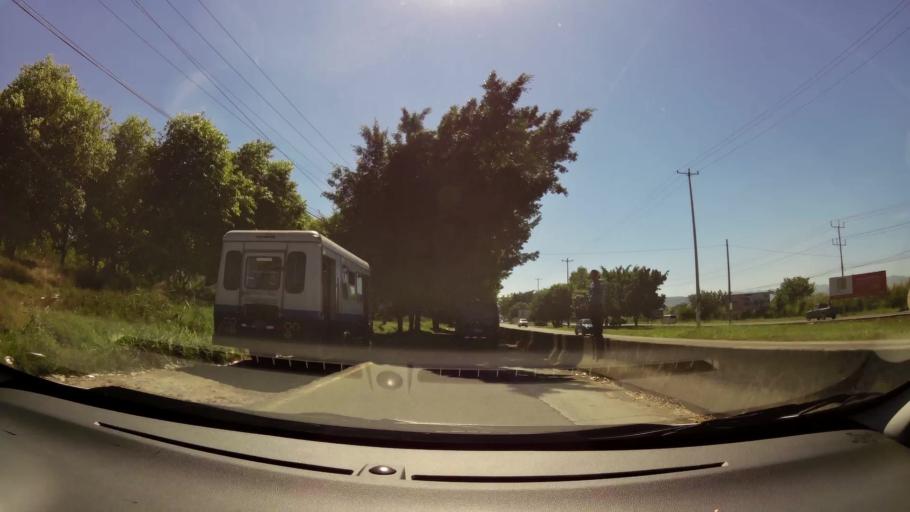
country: SV
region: La Libertad
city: Ciudad Arce
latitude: 13.7798
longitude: -89.3736
